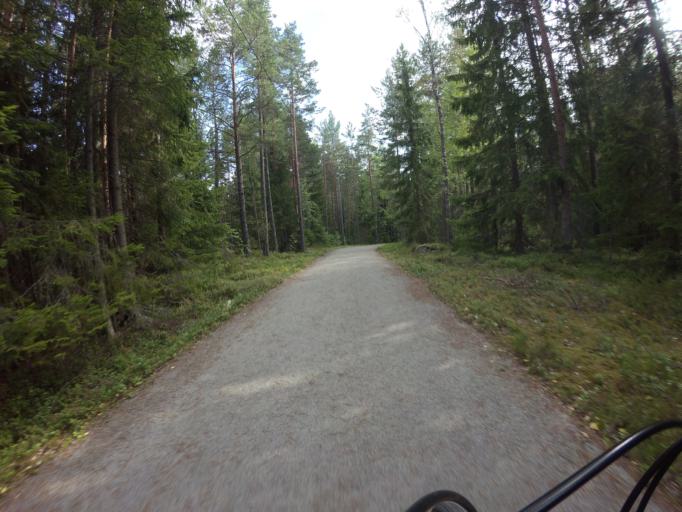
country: FI
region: Varsinais-Suomi
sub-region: Turku
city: Vahto
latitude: 60.5500
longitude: 22.3373
